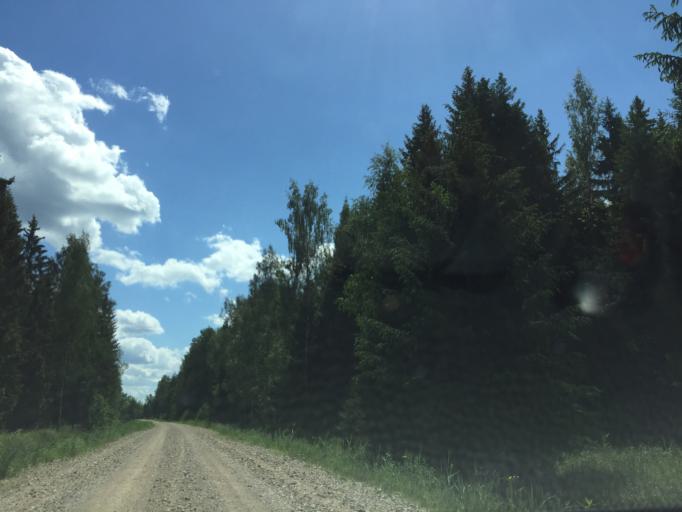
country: LV
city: Tireli
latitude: 56.8494
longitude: 23.6949
